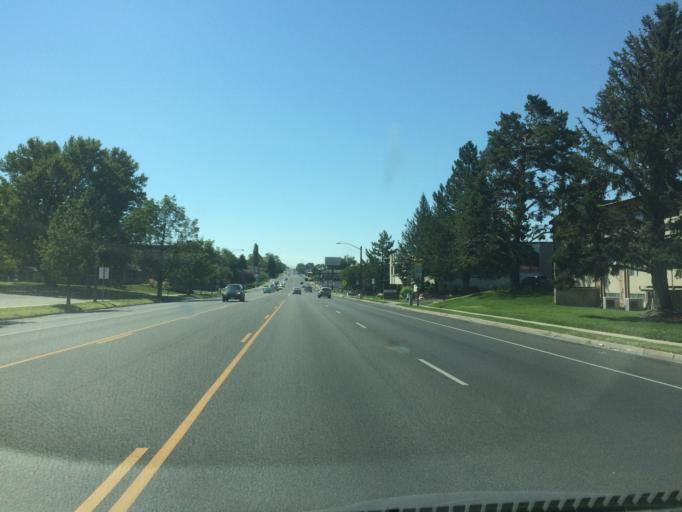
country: US
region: Utah
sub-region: Weber County
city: South Ogden
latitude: 41.2047
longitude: -111.9486
